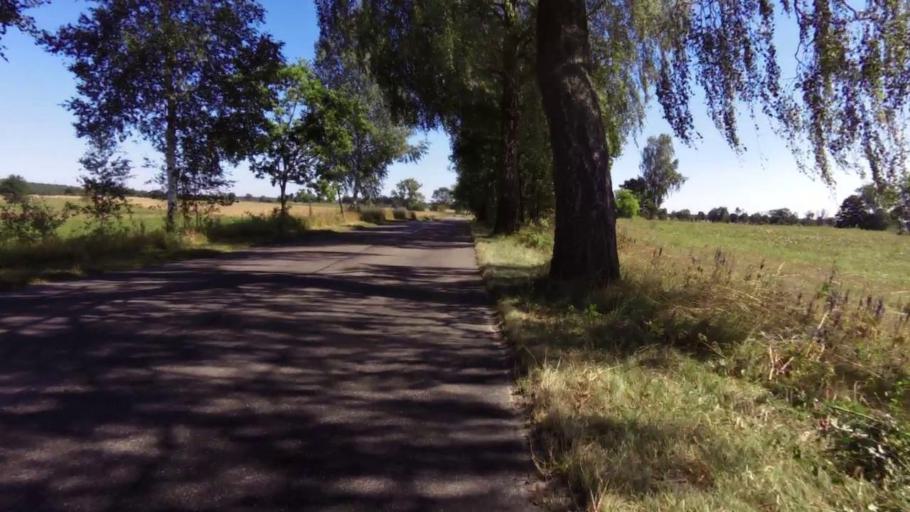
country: PL
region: West Pomeranian Voivodeship
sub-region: Powiat szczecinecki
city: Lubowo
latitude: 53.5847
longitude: 16.4261
